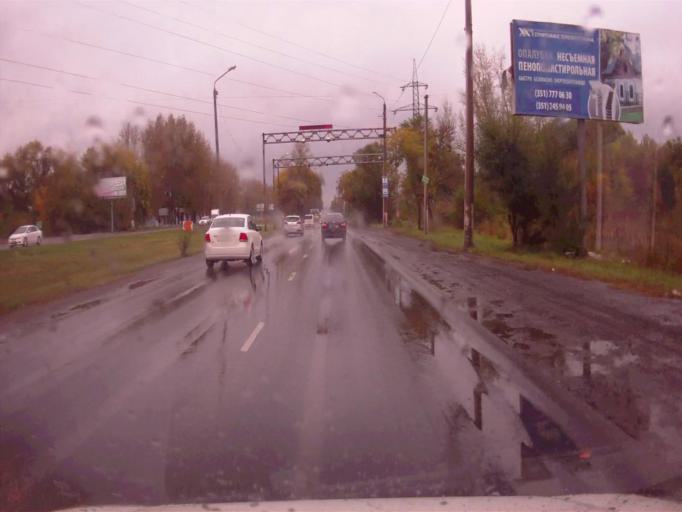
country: RU
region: Chelyabinsk
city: Dolgoderevenskoye
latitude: 55.2484
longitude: 61.3576
